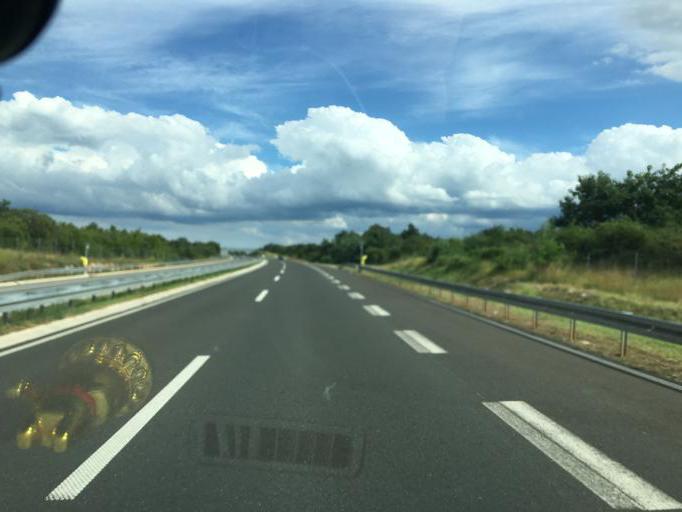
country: HR
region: Istarska
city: Vodnjan
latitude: 45.0945
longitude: 13.8240
